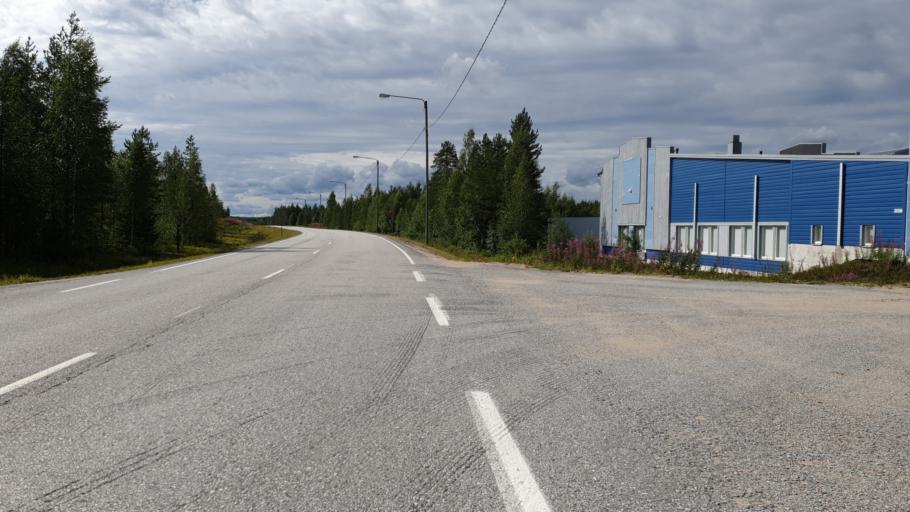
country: FI
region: Kainuu
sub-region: Kehys-Kainuu
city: Kuhmo
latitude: 64.5355
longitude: 29.9442
